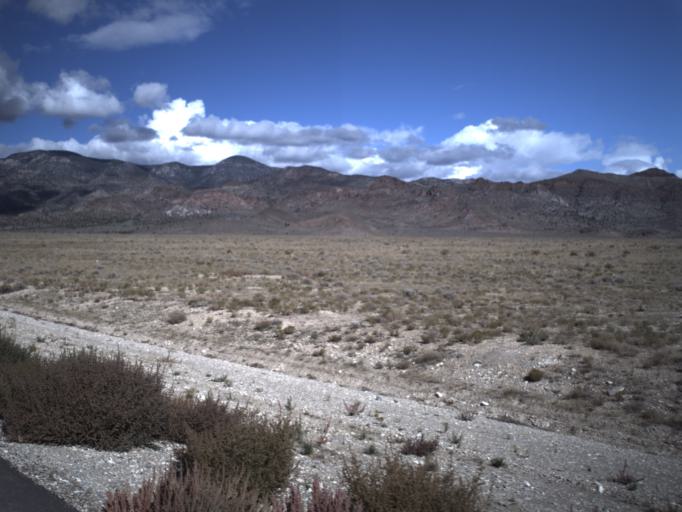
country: US
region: Utah
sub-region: Beaver County
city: Milford
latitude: 38.4902
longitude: -113.4676
